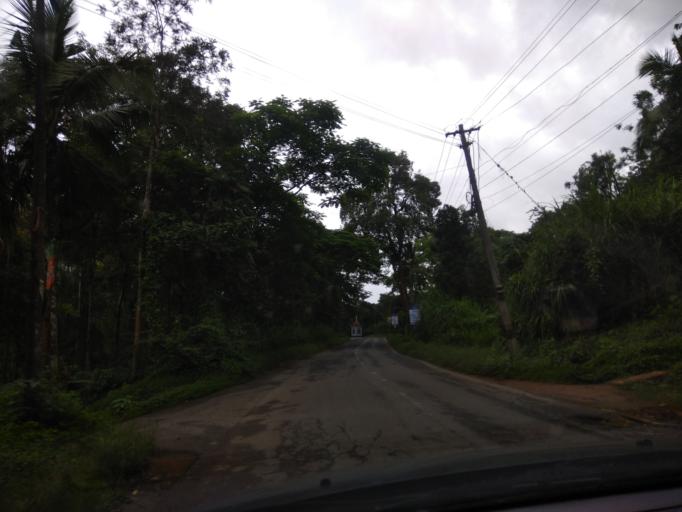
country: IN
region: Kerala
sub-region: Wayanad
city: Panamaram
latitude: 11.8207
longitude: 76.0191
